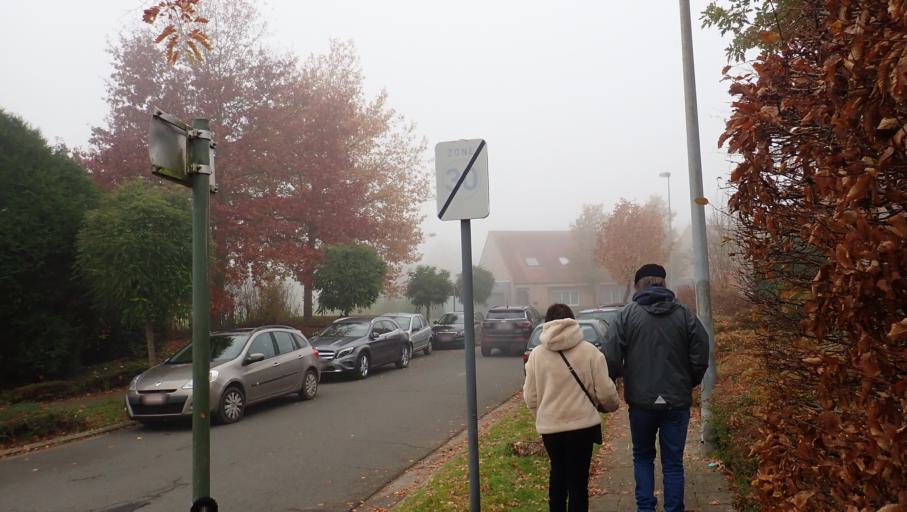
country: BE
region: Flanders
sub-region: Provincie Oost-Vlaanderen
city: Temse
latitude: 51.1314
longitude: 4.2032
